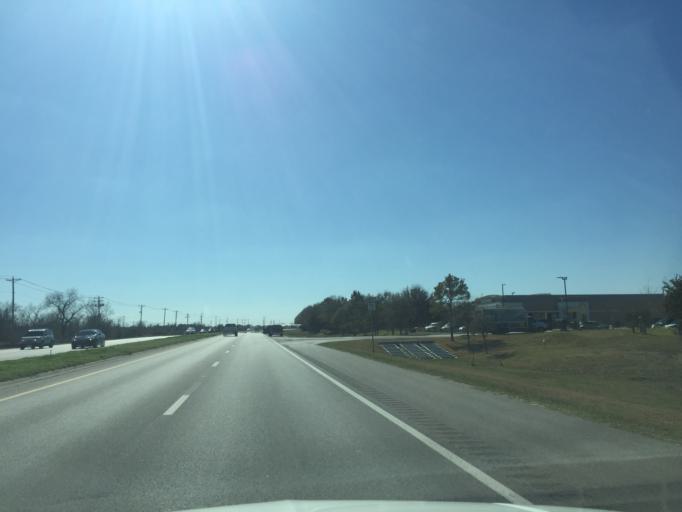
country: US
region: Texas
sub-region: Galveston County
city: Kemah
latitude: 29.5046
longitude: -95.0425
